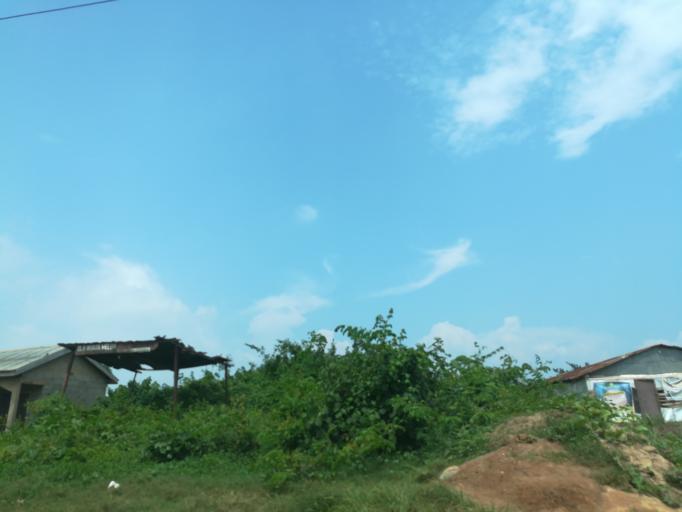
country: NG
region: Lagos
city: Ikorodu
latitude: 6.5881
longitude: 3.6245
